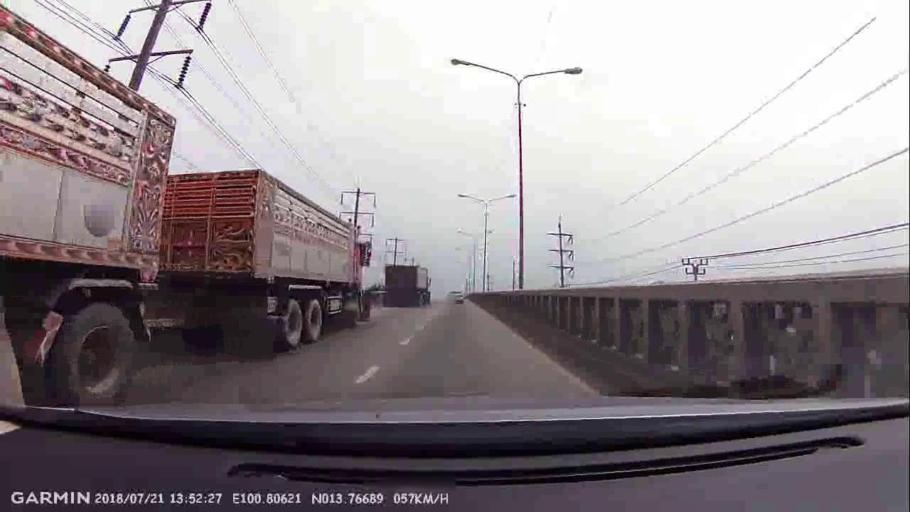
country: TH
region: Bangkok
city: Lat Krabang
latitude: 13.7665
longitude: 100.8063
